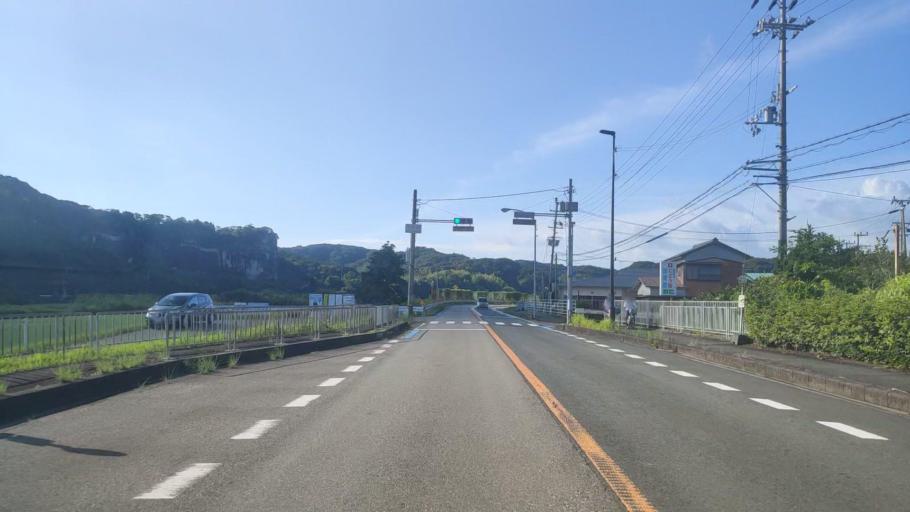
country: JP
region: Wakayama
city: Tanabe
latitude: 33.6611
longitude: 135.3991
